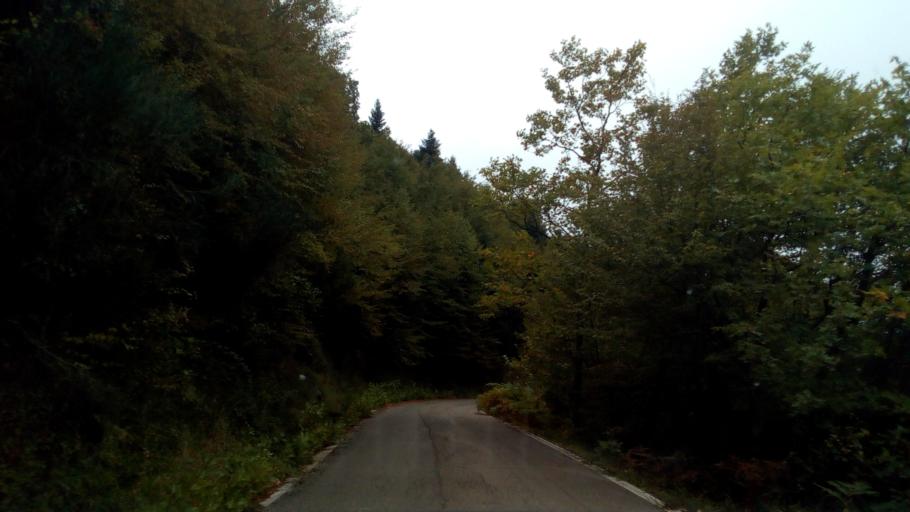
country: GR
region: West Greece
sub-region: Nomos Aitolias kai Akarnanias
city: Thermo
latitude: 38.5895
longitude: 21.8489
